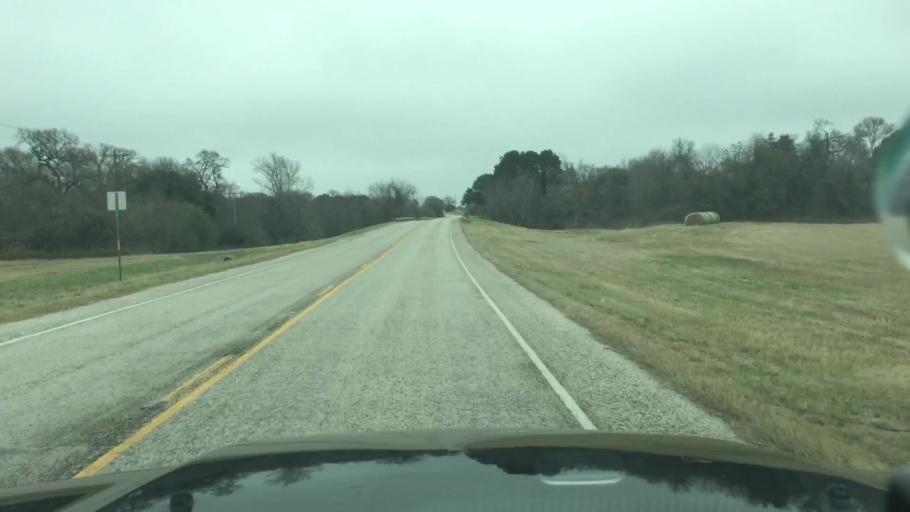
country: US
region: Texas
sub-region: Fayette County
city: La Grange
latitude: 30.0098
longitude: -96.9113
